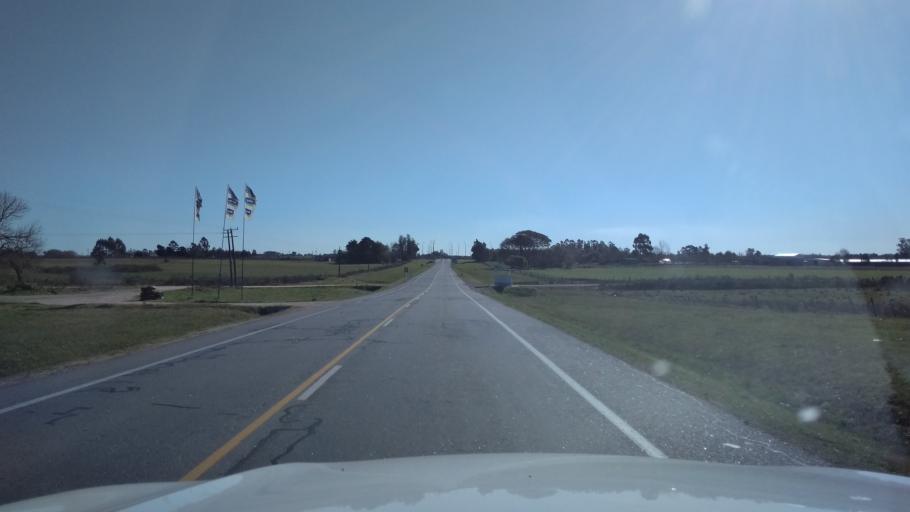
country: UY
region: Canelones
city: San Jacinto
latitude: -34.5307
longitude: -55.9462
